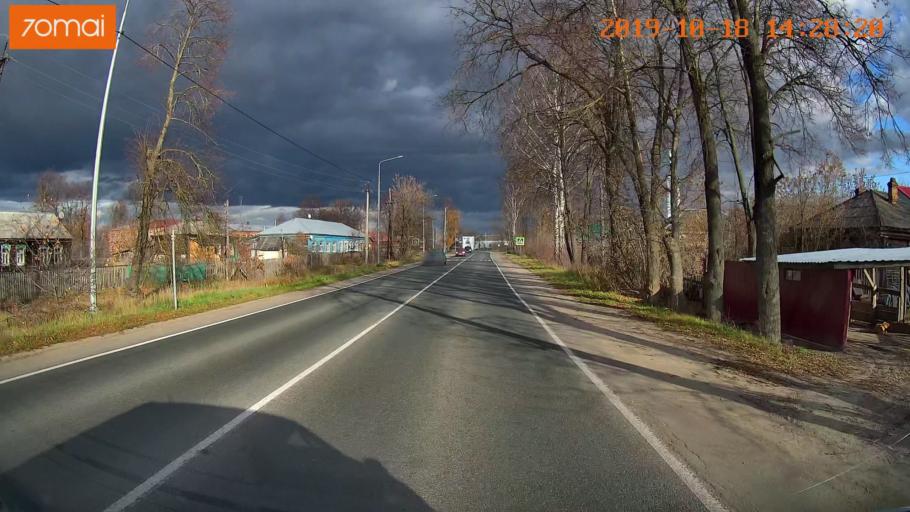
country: RU
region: Rjazan
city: Tuma
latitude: 55.1482
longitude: 40.5508
